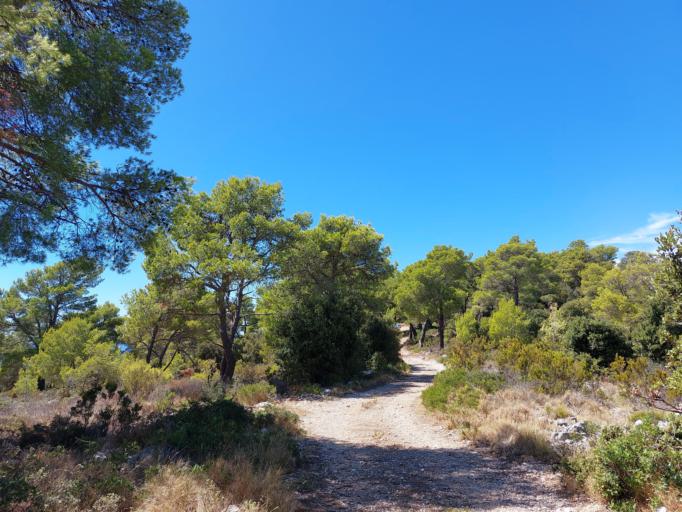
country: HR
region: Dubrovacko-Neretvanska
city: Smokvica
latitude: 42.7420
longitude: 16.8390
